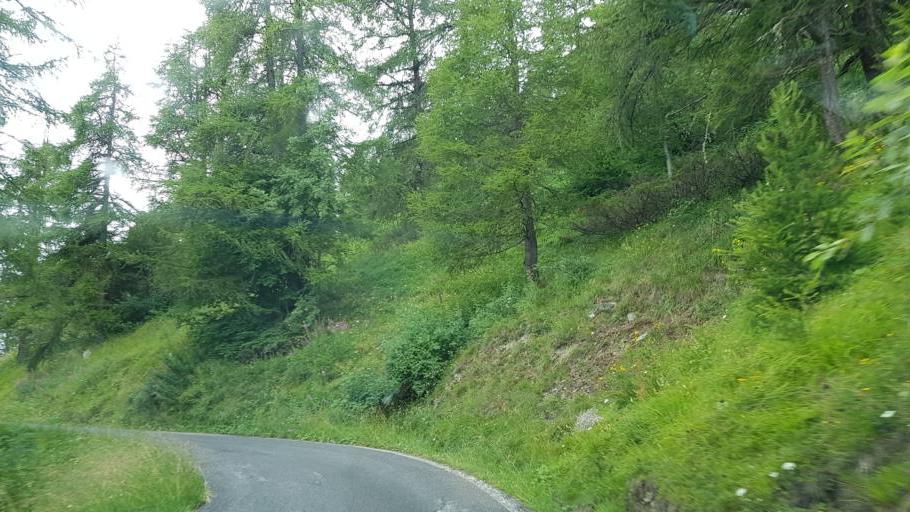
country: IT
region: Piedmont
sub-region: Provincia di Cuneo
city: Stroppo
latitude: 44.5160
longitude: 7.1059
